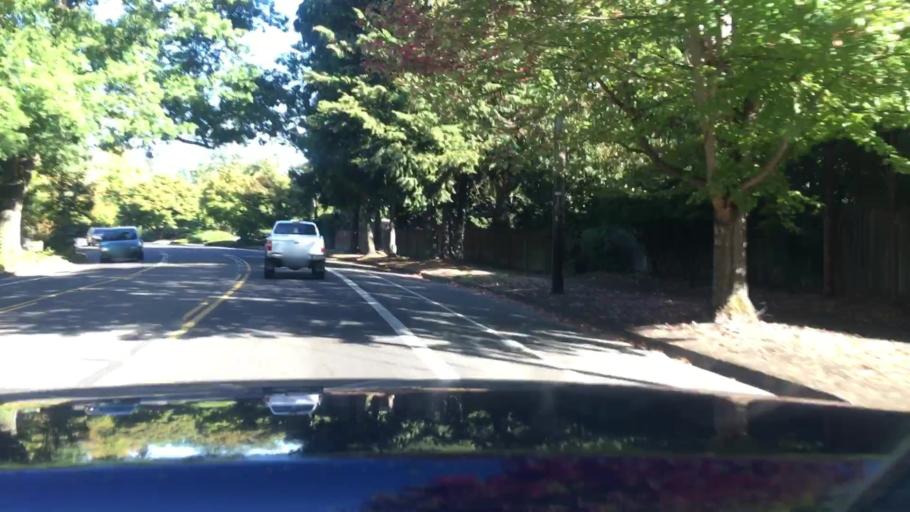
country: US
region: Oregon
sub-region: Lane County
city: Eugene
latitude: 44.0693
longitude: -123.0664
